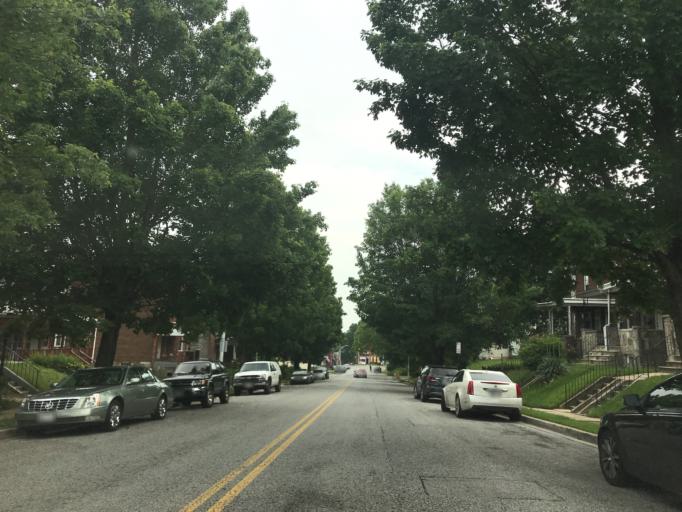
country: US
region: Maryland
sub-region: City of Baltimore
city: Baltimore
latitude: 39.3115
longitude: -76.6642
